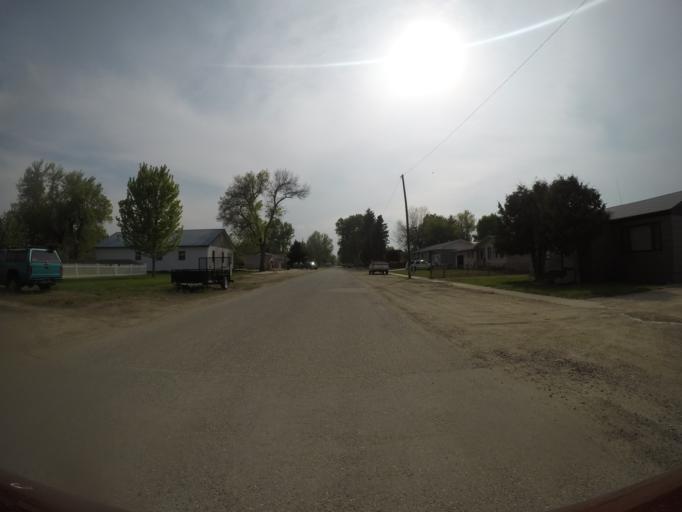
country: US
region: Montana
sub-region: Yellowstone County
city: Laurel
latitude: 45.4829
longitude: -108.9744
